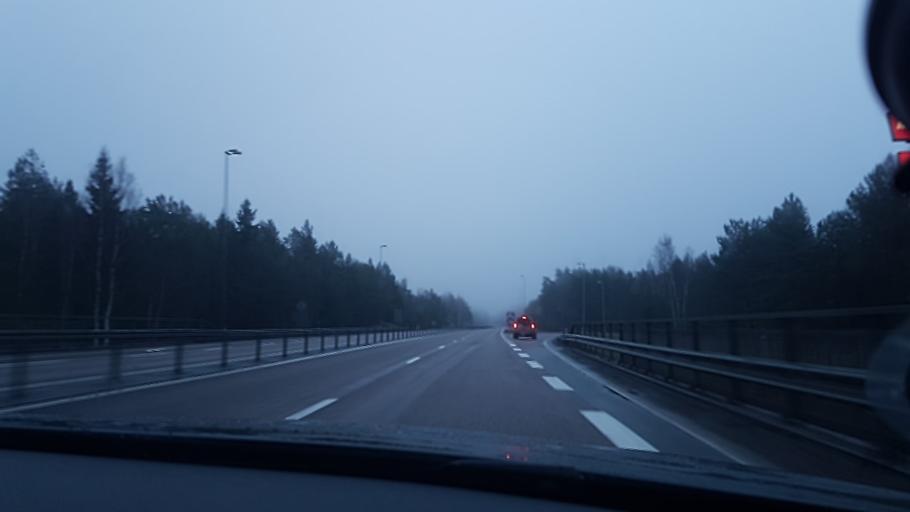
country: SE
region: Vaermland
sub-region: Kristinehamns Kommun
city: Kristinehamn
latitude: 59.3171
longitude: 14.1496
